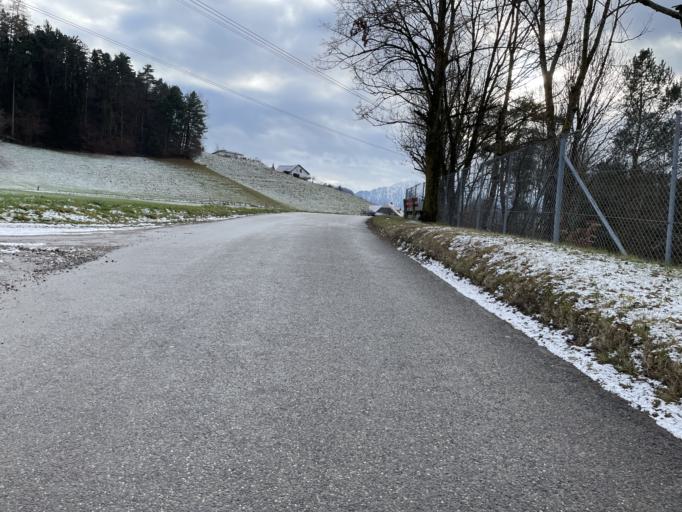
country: CH
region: Lucerne
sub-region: Entlebuch District
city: Oberdiessbach
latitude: 46.8276
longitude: 7.6157
